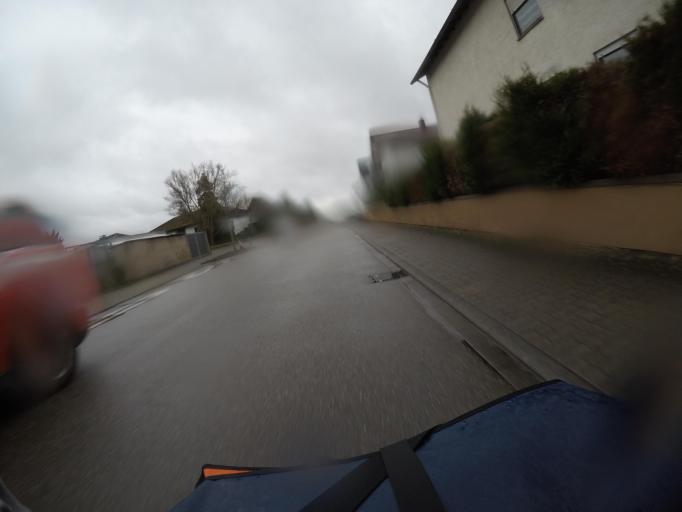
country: DE
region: Baden-Wuerttemberg
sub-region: Karlsruhe Region
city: Graben-Neudorf
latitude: 49.1084
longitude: 8.4728
